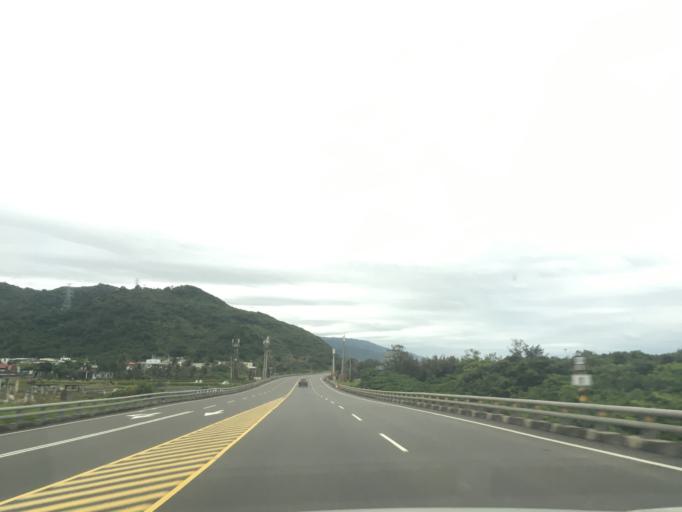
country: TW
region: Taiwan
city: Hengchun
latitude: 22.3053
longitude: 120.8898
